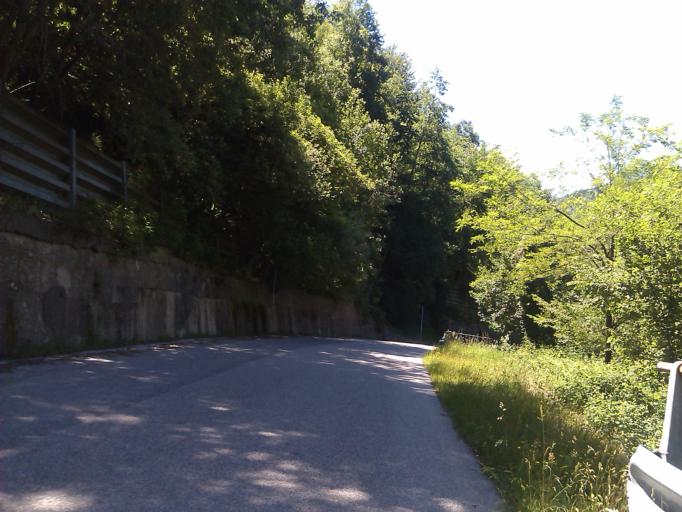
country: IT
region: Tuscany
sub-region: Provincia di Prato
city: Cantagallo
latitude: 44.0440
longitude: 11.0404
